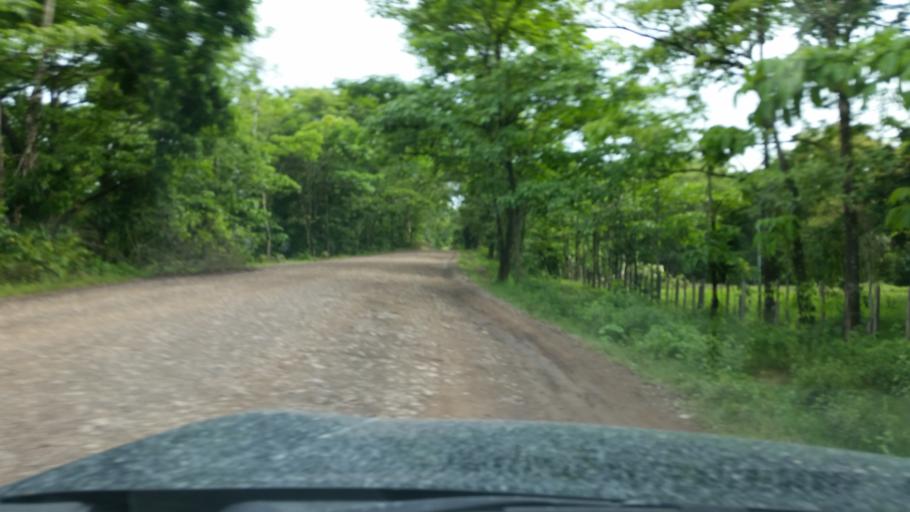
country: NI
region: Atlantico Norte (RAAN)
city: Siuna
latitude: 13.4570
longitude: -84.8499
